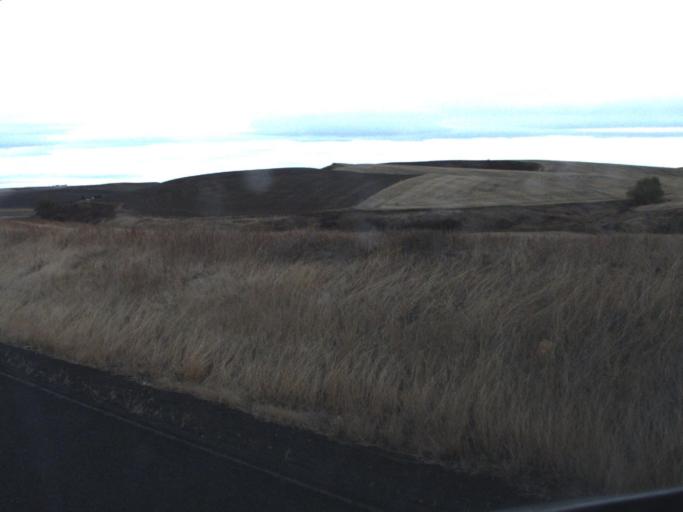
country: US
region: Washington
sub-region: Whitman County
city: Pullman
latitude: 46.5872
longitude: -117.1644
